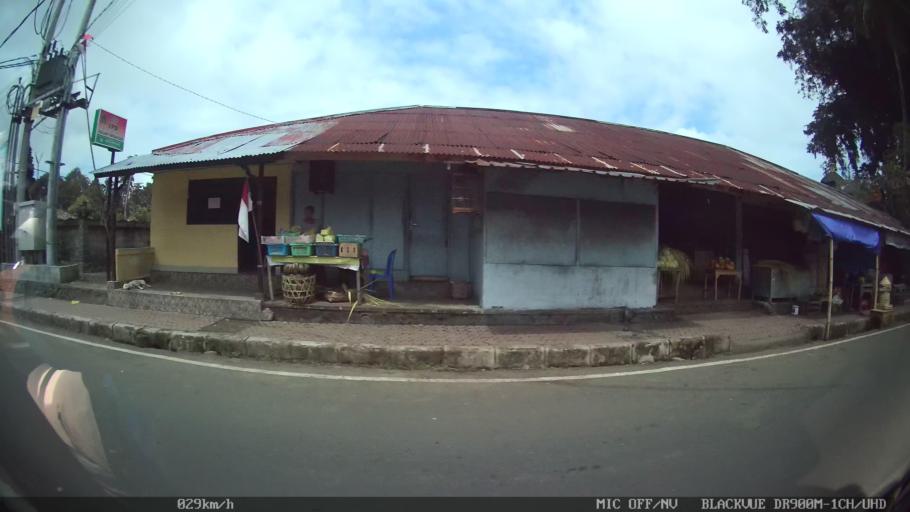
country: ID
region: Bali
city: Banjar Kubu
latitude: -8.4465
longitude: 115.3957
